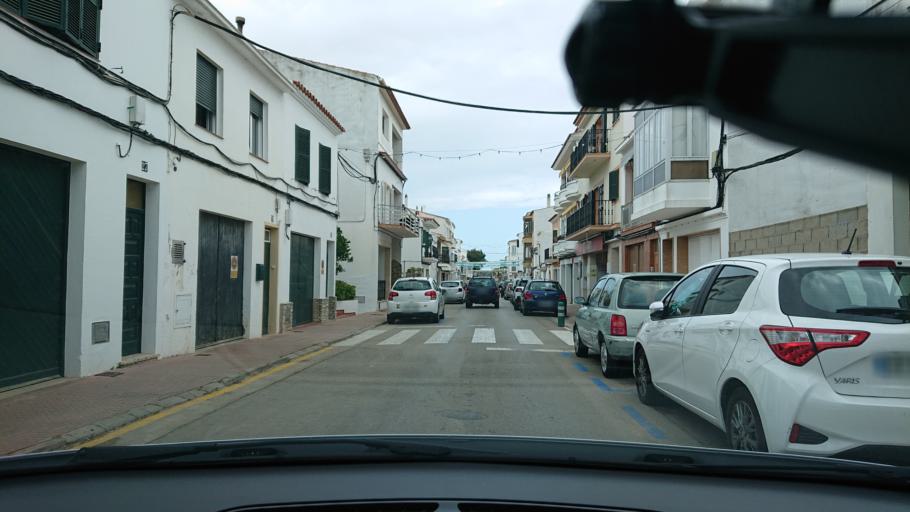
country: ES
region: Balearic Islands
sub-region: Illes Balears
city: Mercadal
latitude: 39.9894
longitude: 4.0936
